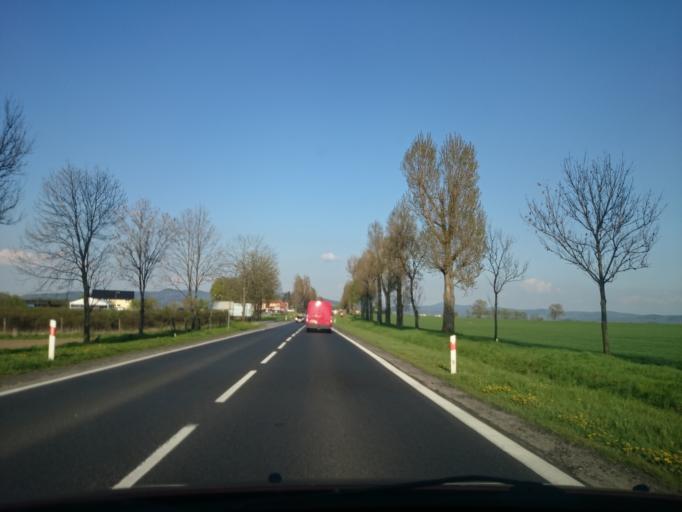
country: PL
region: Lower Silesian Voivodeship
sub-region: Powiat klodzki
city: Klodzko
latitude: 50.4373
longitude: 16.6040
